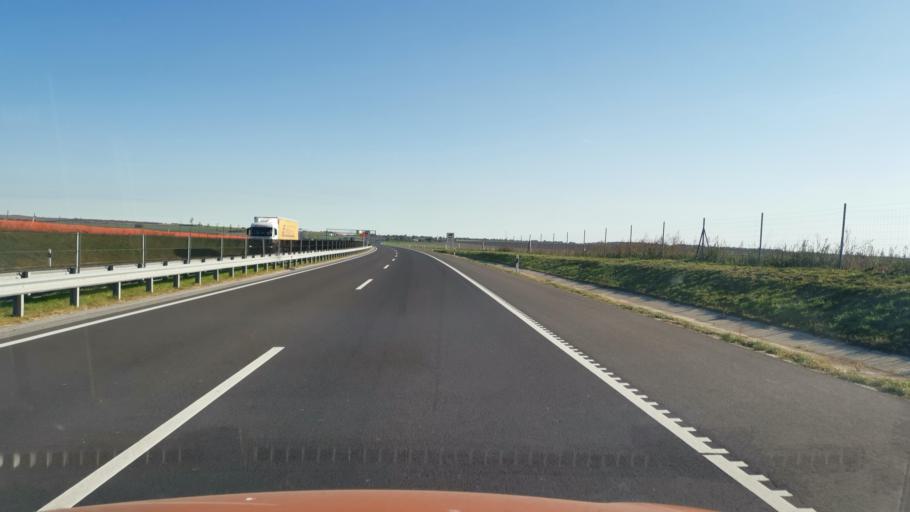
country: HU
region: Borsod-Abauj-Zemplen
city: Arnot
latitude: 48.1487
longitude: 20.8610
